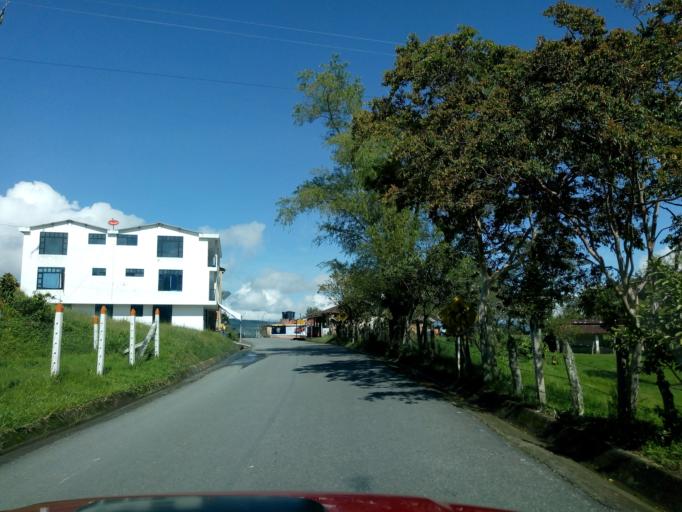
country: CO
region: Boyaca
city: Moniquira
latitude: 5.8708
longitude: -73.5542
